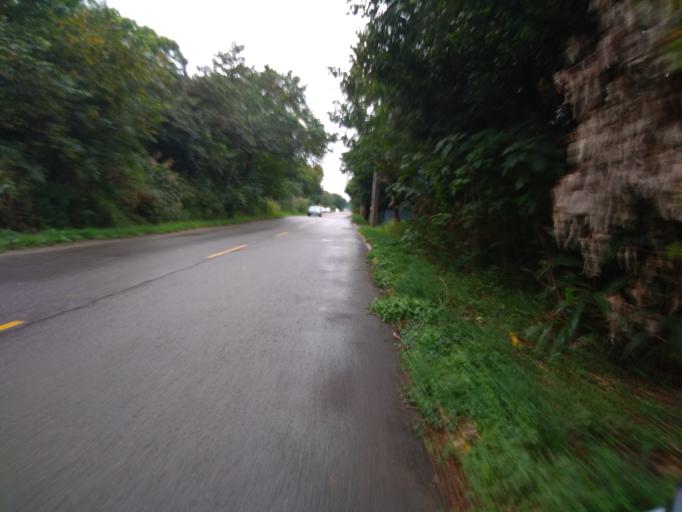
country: TW
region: Taiwan
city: Daxi
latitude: 24.9330
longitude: 121.1836
